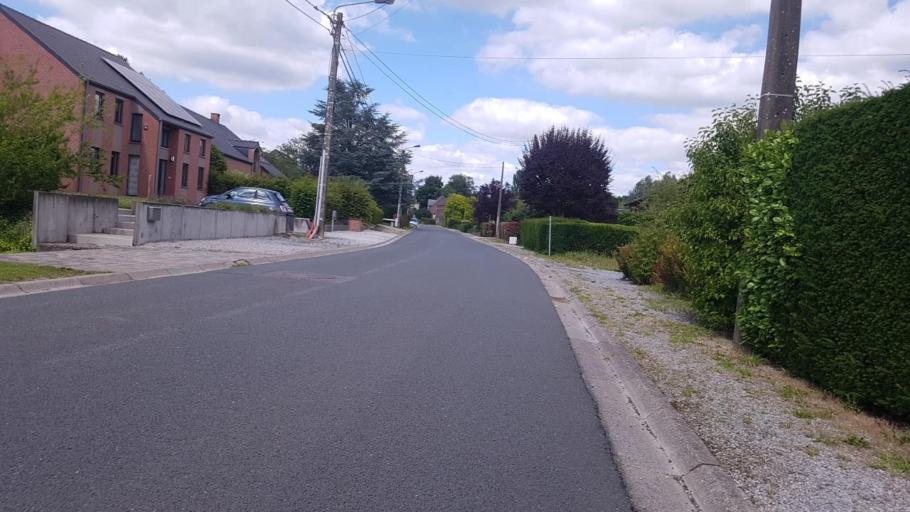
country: BE
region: Wallonia
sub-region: Province du Hainaut
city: Charleroi
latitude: 50.3353
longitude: 4.3904
